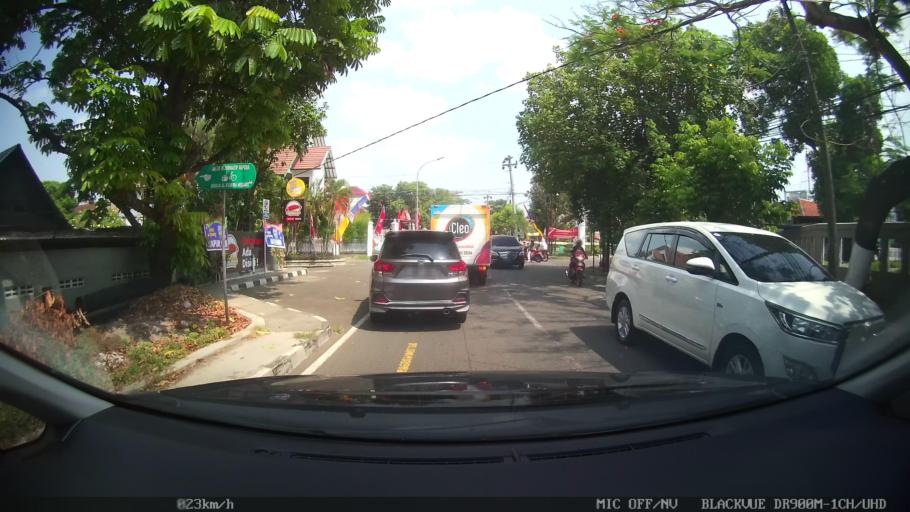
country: ID
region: Daerah Istimewa Yogyakarta
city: Yogyakarta
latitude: -7.8004
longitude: 110.3944
